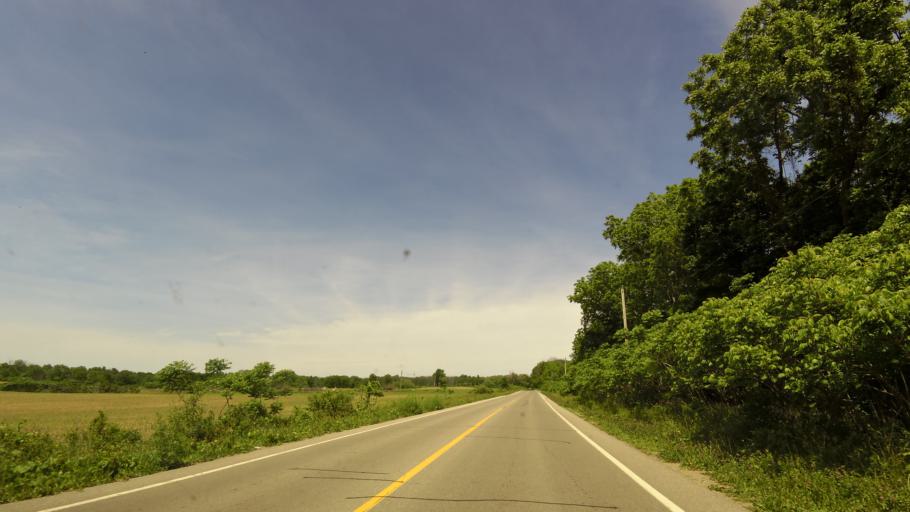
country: CA
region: Ontario
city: Norfolk County
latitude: 42.6814
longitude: -80.3646
